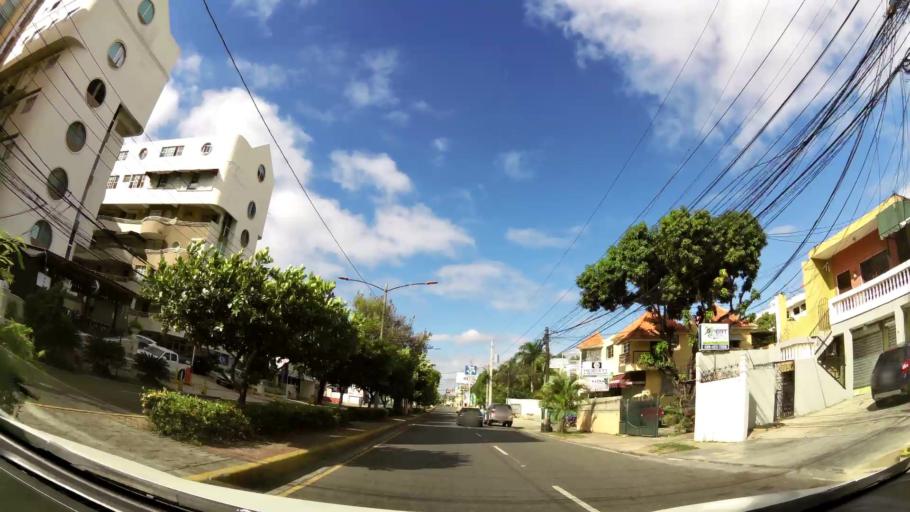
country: DO
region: Nacional
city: La Julia
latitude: 18.4598
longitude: -69.9350
